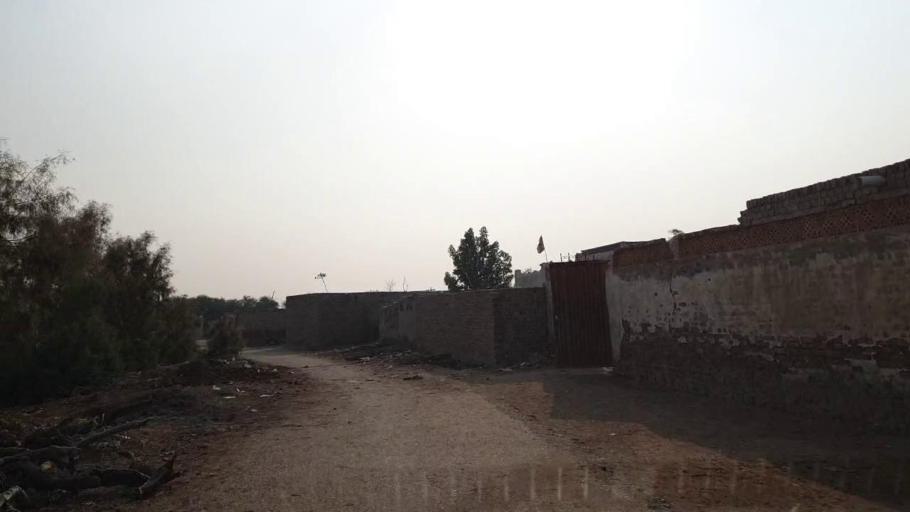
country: PK
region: Sindh
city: Bhan
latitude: 26.4728
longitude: 67.7263
